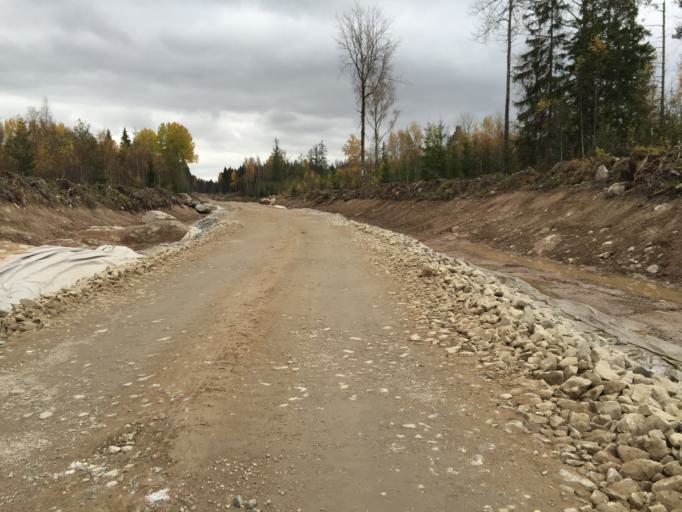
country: SE
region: Vaestmanland
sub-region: Hallstahammars Kommun
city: Hallstahammar
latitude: 59.6359
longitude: 16.2079
